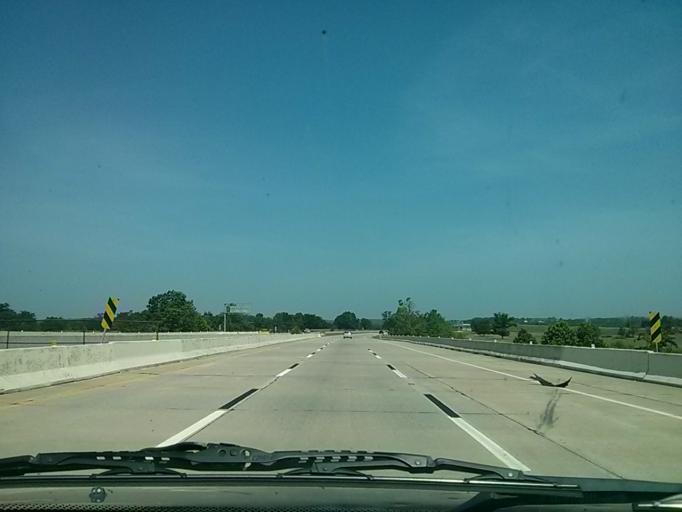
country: US
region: Oklahoma
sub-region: Creek County
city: Sapulpa
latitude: 36.0204
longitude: -96.0699
